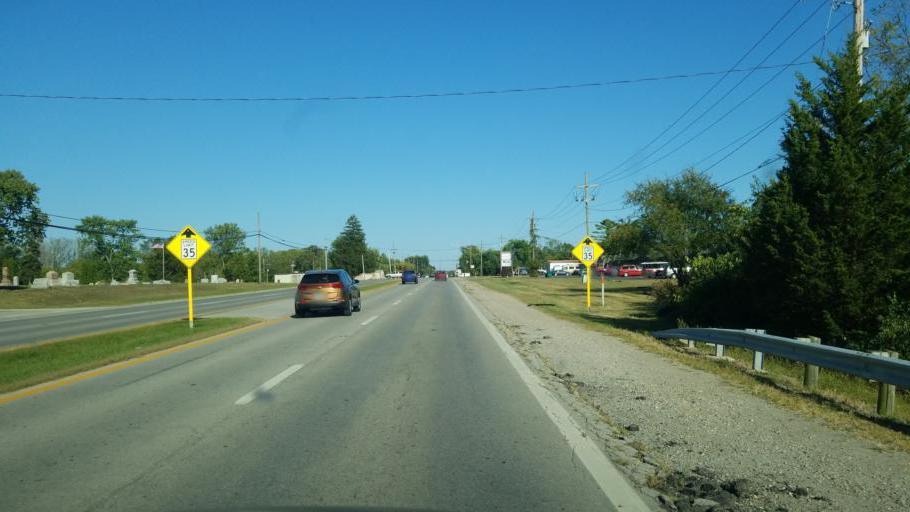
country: US
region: Ohio
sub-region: Madison County
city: West Jefferson
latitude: 39.9438
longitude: -83.2870
